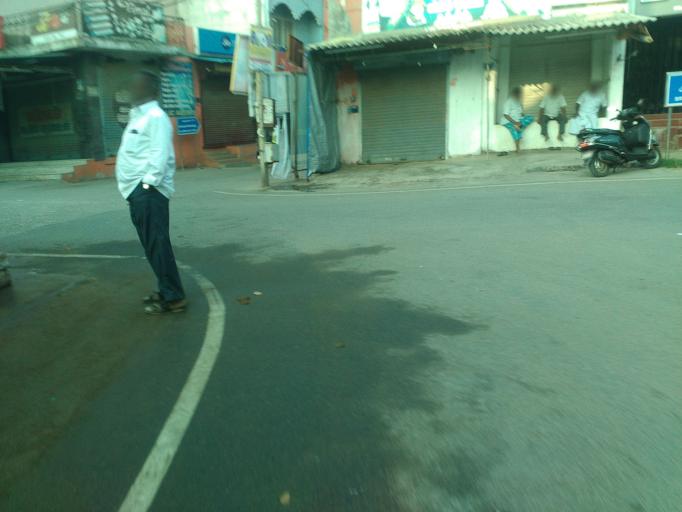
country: IN
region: Tamil Nadu
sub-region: Vellore
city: Ambur
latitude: 12.7861
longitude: 78.7165
